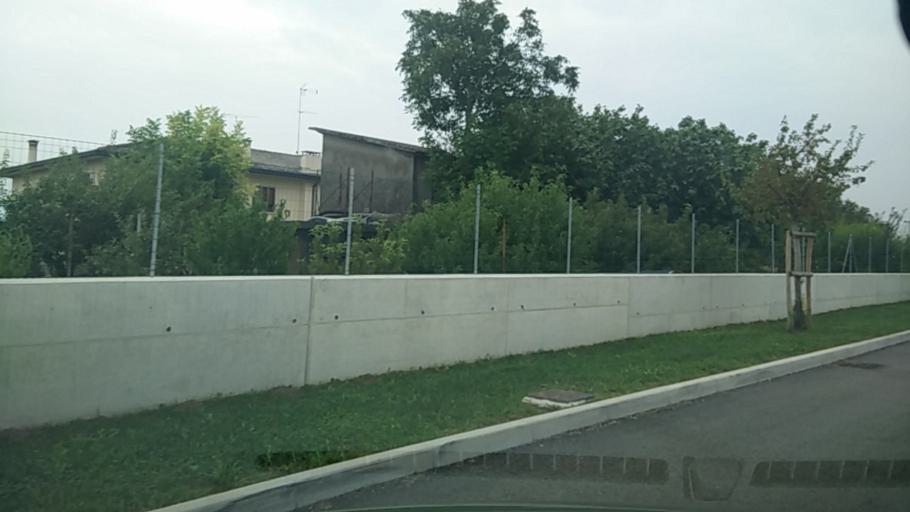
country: IT
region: Veneto
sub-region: Provincia di Venezia
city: Noventa di Piave
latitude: 45.6732
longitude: 12.5398
